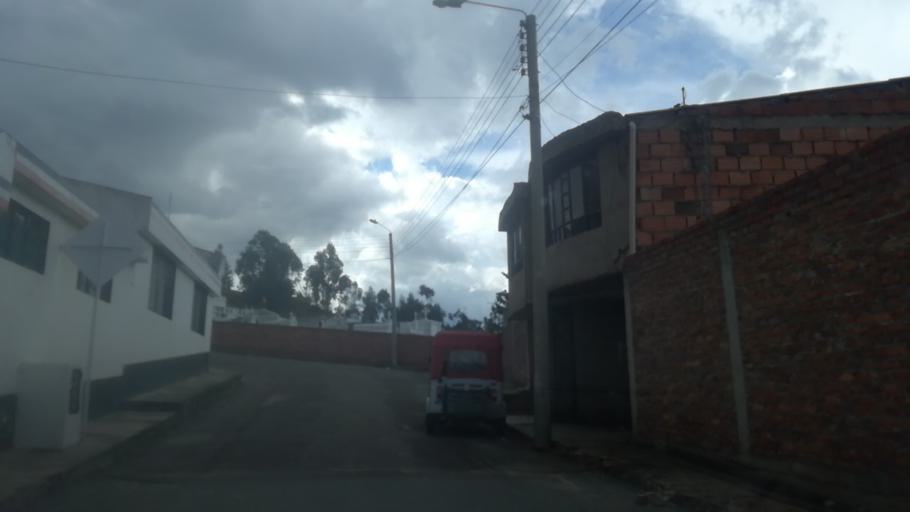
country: CO
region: Boyaca
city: Socha Viejo
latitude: 5.9974
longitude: -72.6949
